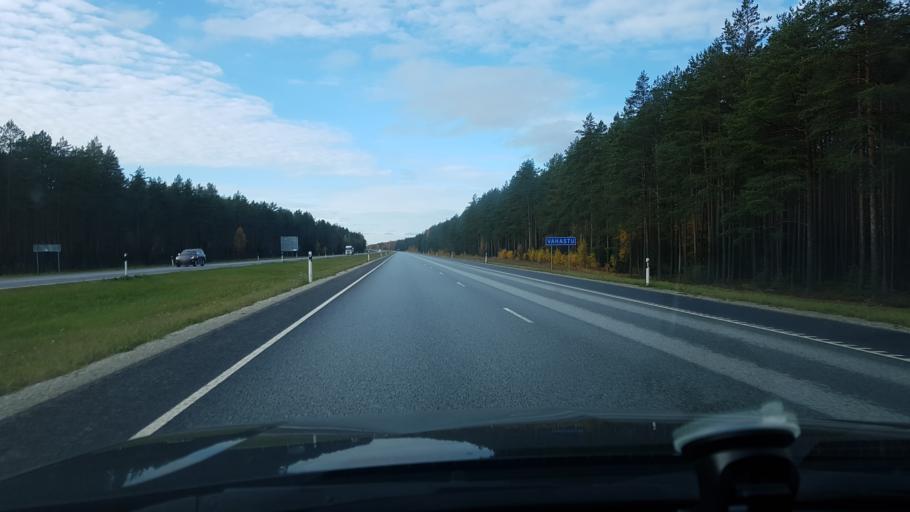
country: EE
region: Harju
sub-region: Loksa linn
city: Loksa
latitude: 59.4623
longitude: 25.6315
